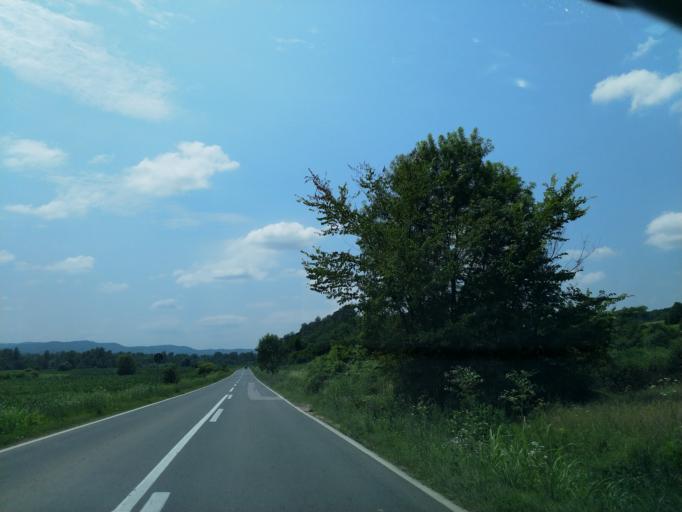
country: RS
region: Central Serbia
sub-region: Rasinski Okrug
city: Krusevac
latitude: 43.4851
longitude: 21.2764
